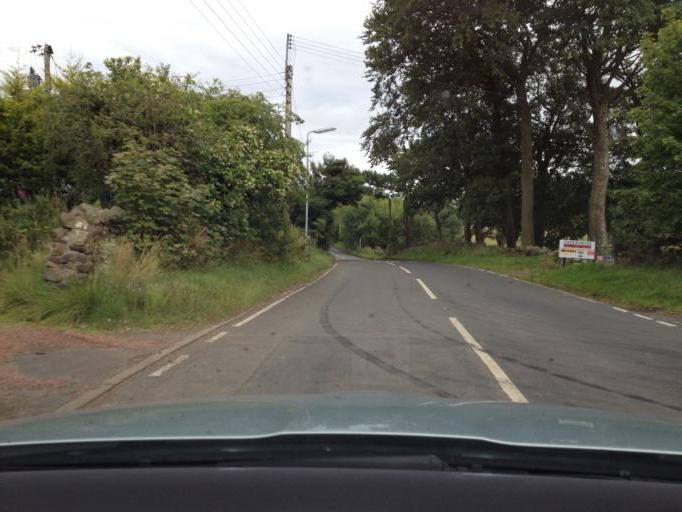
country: GB
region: Scotland
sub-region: West Lothian
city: Armadale
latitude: 55.9298
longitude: -3.7409
